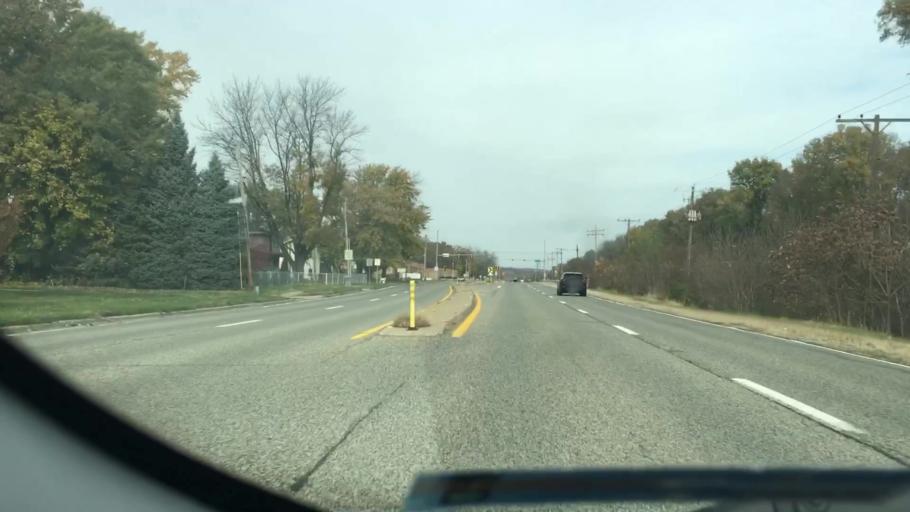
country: US
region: Illinois
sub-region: Peoria County
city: Peoria Heights
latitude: 40.7567
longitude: -89.5638
